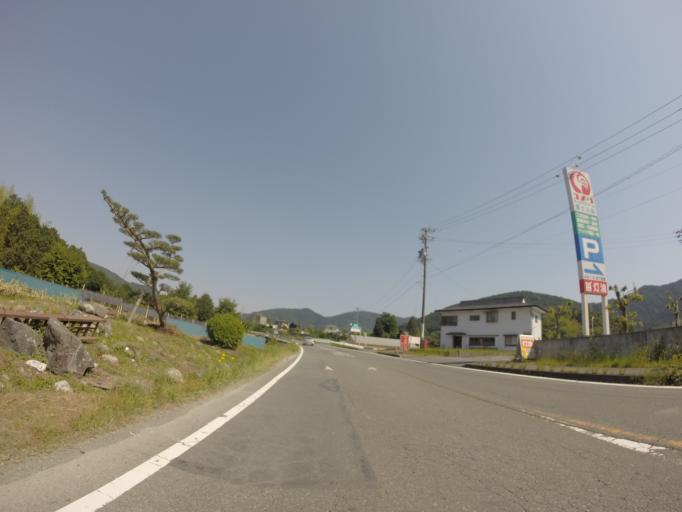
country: JP
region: Shizuoka
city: Fujinomiya
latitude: 35.1898
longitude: 138.5910
